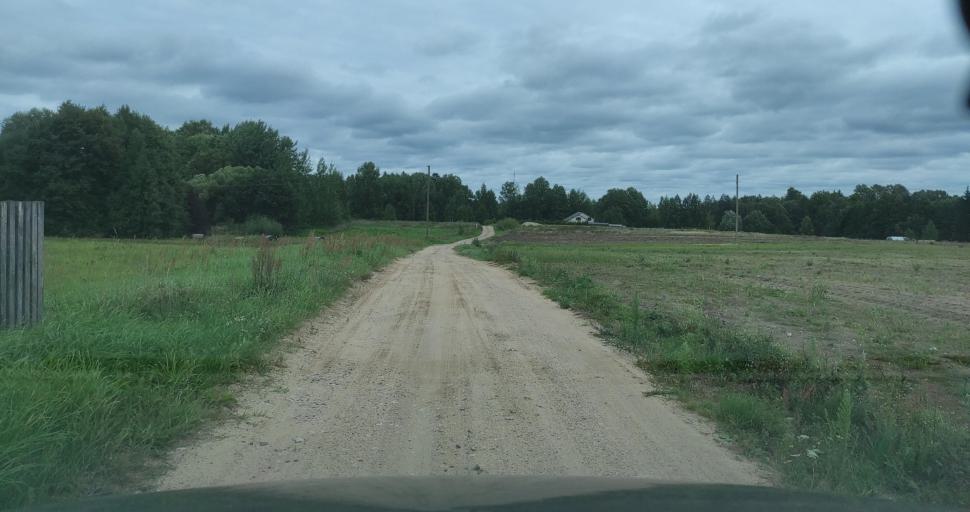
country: LV
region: Kuldigas Rajons
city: Kuldiga
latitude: 56.9265
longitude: 21.9645
